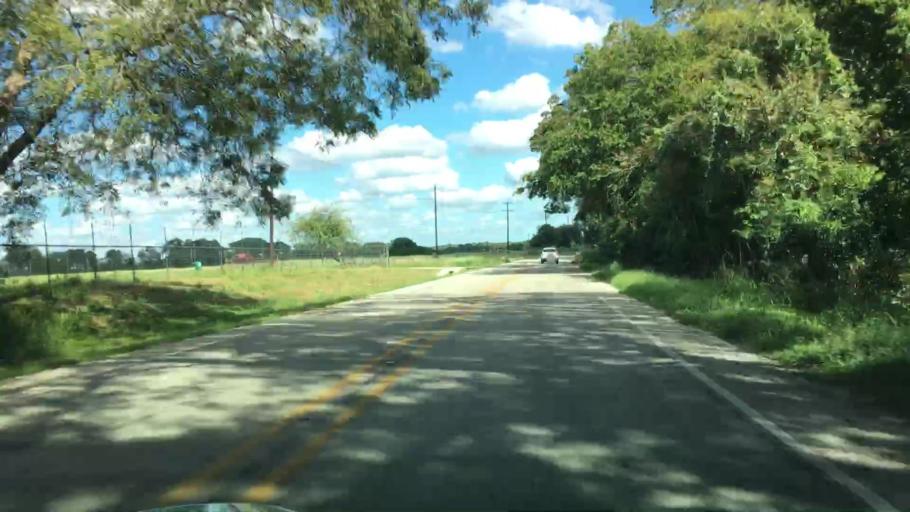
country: US
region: Texas
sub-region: Blanco County
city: Blanco
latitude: 30.0921
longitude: -98.3934
